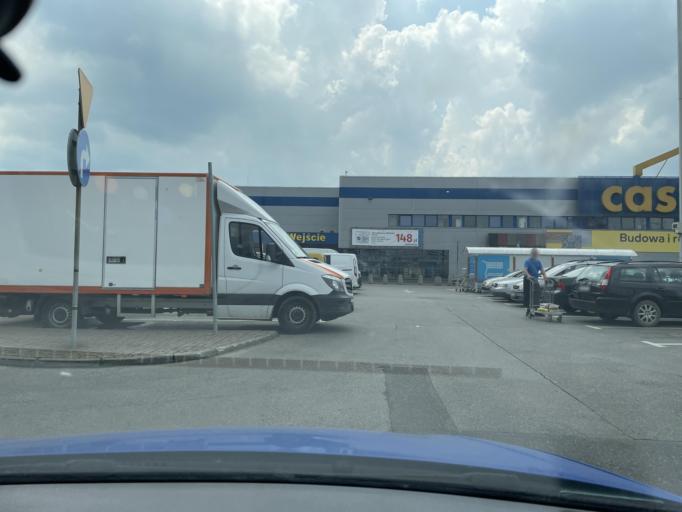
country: PL
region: Silesian Voivodeship
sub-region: Katowice
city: Katowice
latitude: 50.2685
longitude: 19.0616
